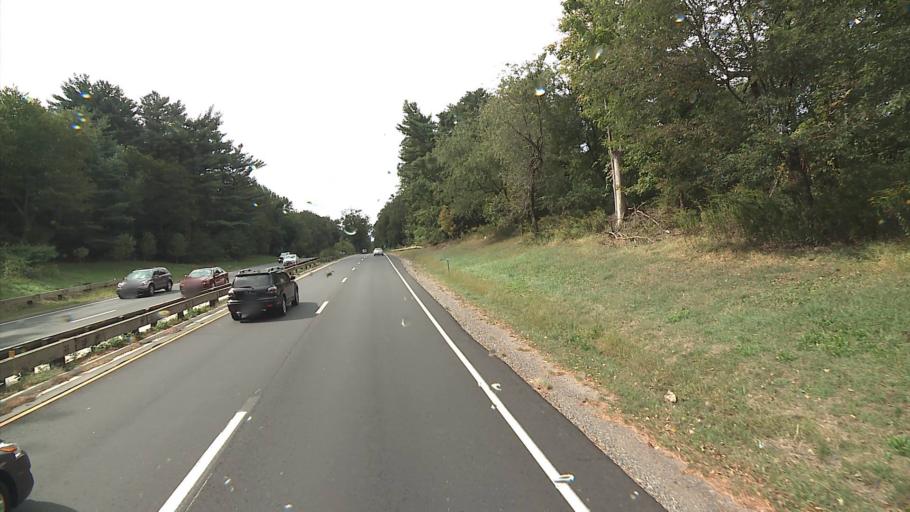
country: US
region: Connecticut
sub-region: Fairfield County
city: North Stamford
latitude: 41.1161
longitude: -73.5355
